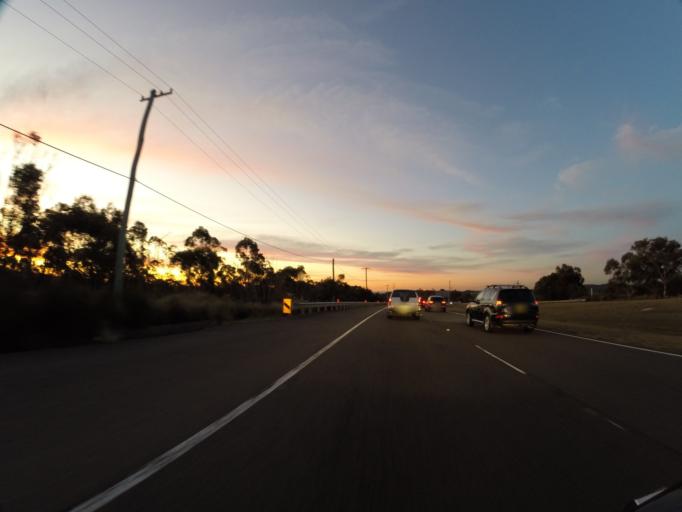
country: AU
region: New South Wales
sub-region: Sutherland Shire
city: Heathcote
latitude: -34.1059
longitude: 150.9935
